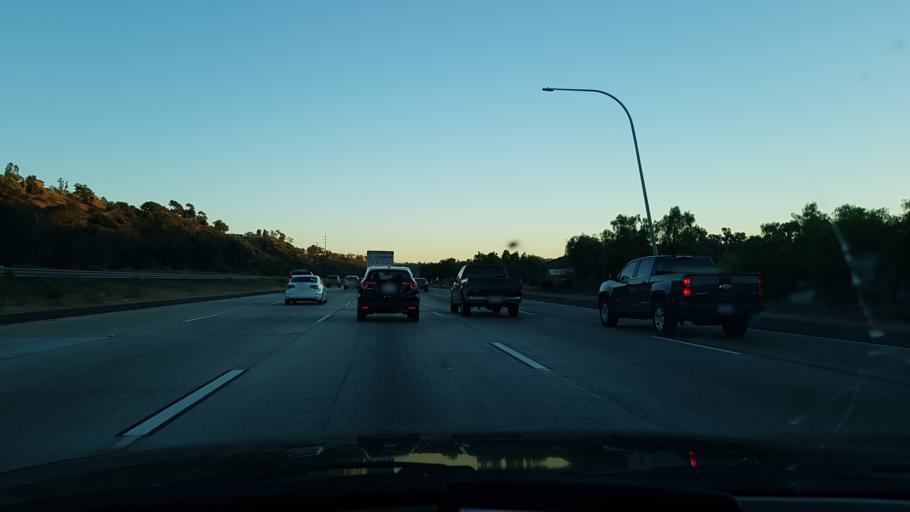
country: US
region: California
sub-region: San Diego County
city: La Mesa
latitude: 32.8066
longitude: -117.1137
